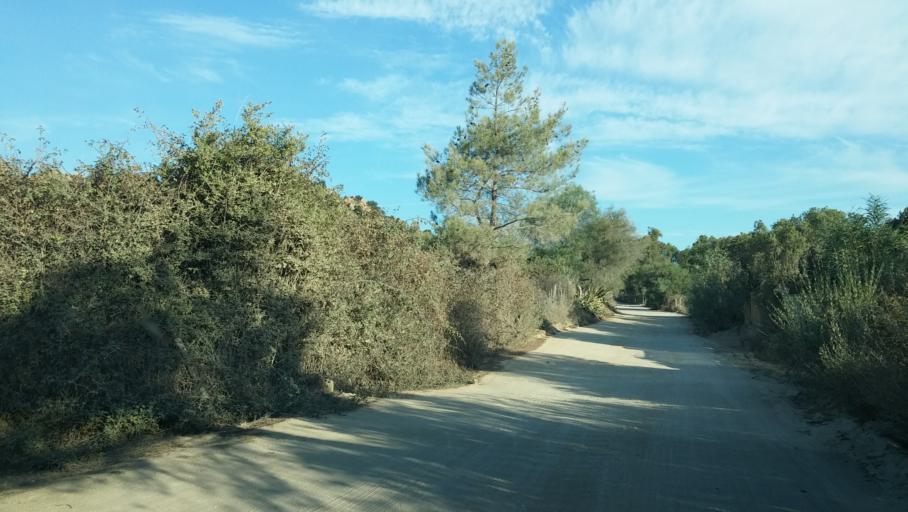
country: IT
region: Sardinia
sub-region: Provincia di Nuoro
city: La Caletta
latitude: 40.4850
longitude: 9.8013
